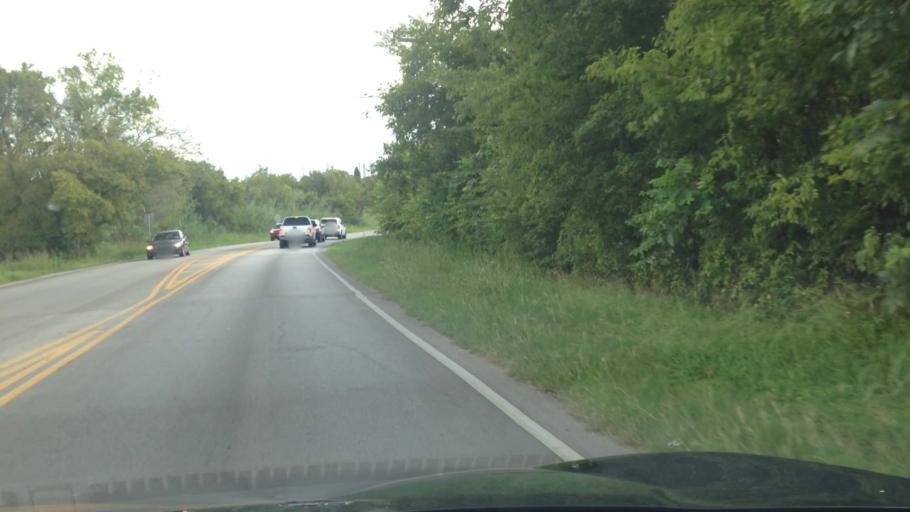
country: US
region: Texas
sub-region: Bexar County
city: Live Oak
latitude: 29.5820
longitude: -98.4034
